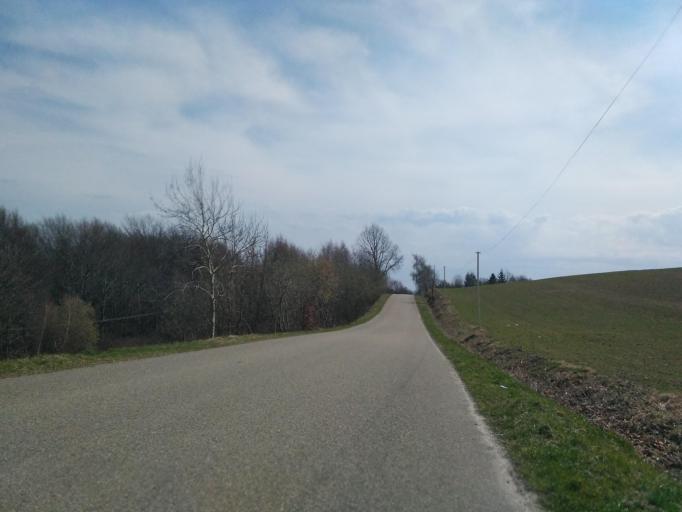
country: PL
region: Subcarpathian Voivodeship
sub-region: Powiat ropczycko-sedziszowski
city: Iwierzyce
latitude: 49.9790
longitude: 21.7443
